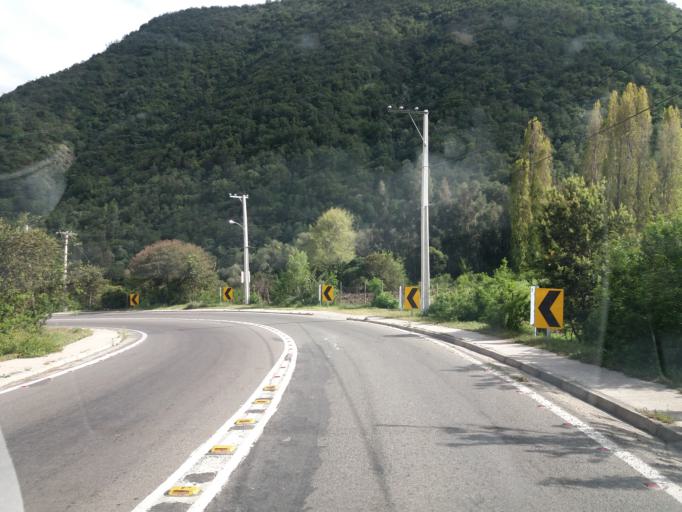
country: CL
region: Valparaiso
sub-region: Provincia de Marga Marga
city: Limache
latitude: -33.0631
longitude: -71.0657
